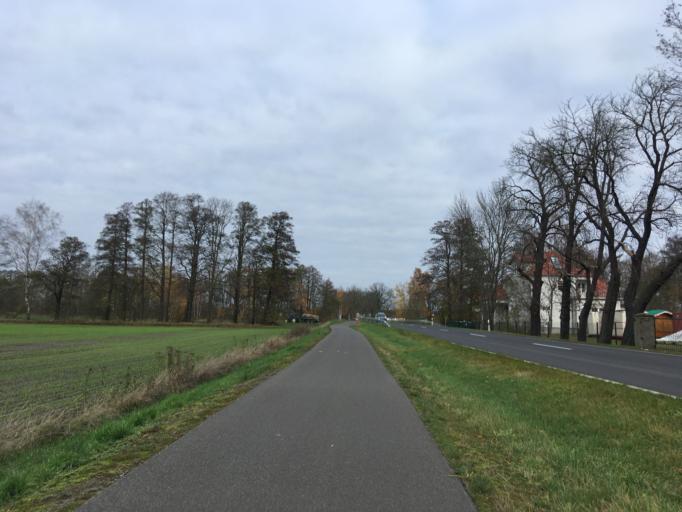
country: DE
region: Brandenburg
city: Peitz
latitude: 51.8750
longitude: 14.4187
